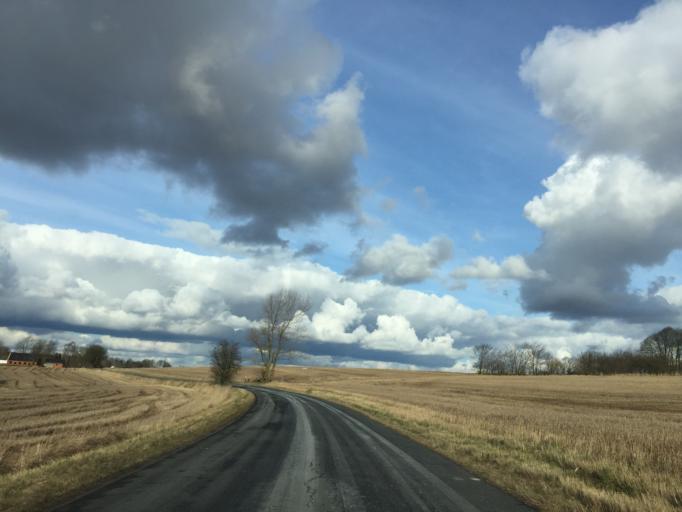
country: DK
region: Central Jutland
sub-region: Favrskov Kommune
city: Hammel
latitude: 56.1972
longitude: 9.8107
